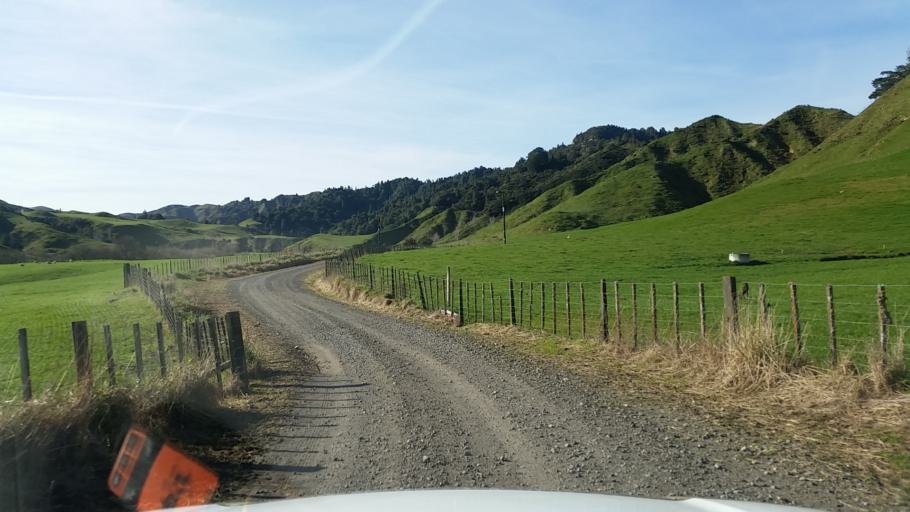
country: NZ
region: Taranaki
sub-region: South Taranaki District
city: Eltham
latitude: -39.3105
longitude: 174.5439
